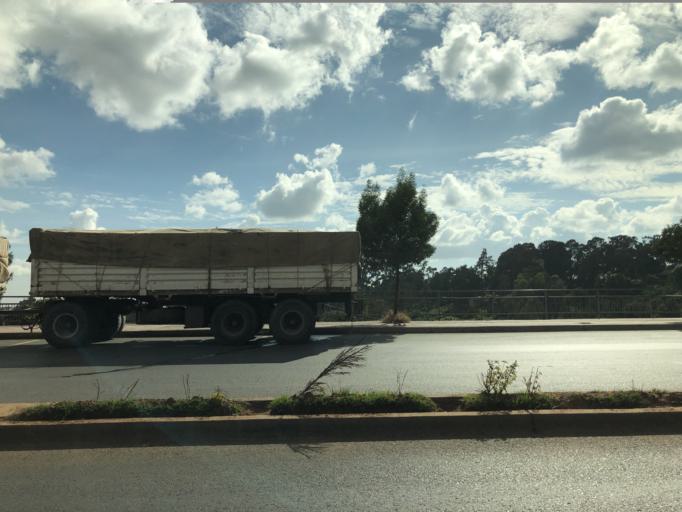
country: ET
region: Adis Abeba
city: Addis Ababa
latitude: 9.0316
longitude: 38.7699
